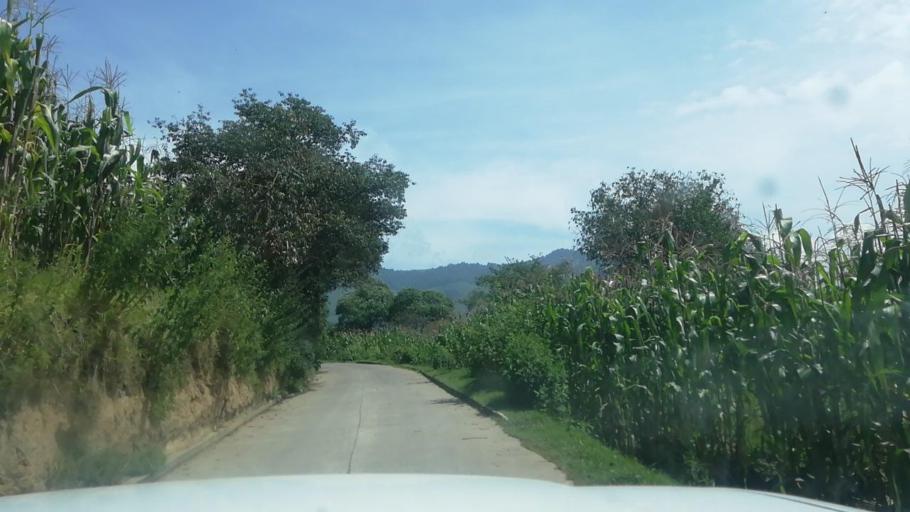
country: GT
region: Totonicapan
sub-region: Municipio de San Andres Xecul
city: San Andres Xecul
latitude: 14.8922
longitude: -91.4745
